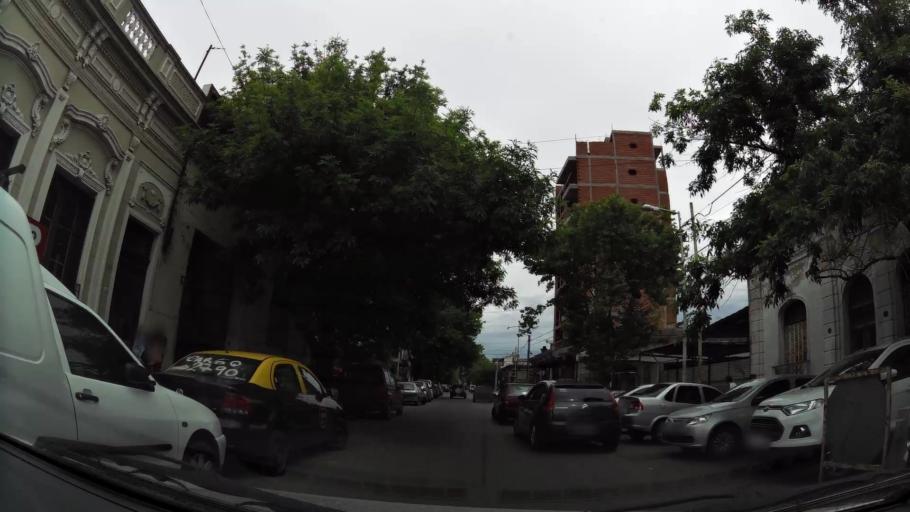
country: AR
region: Buenos Aires
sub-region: Partido de Avellaneda
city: Avellaneda
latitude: -34.6641
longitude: -58.3681
